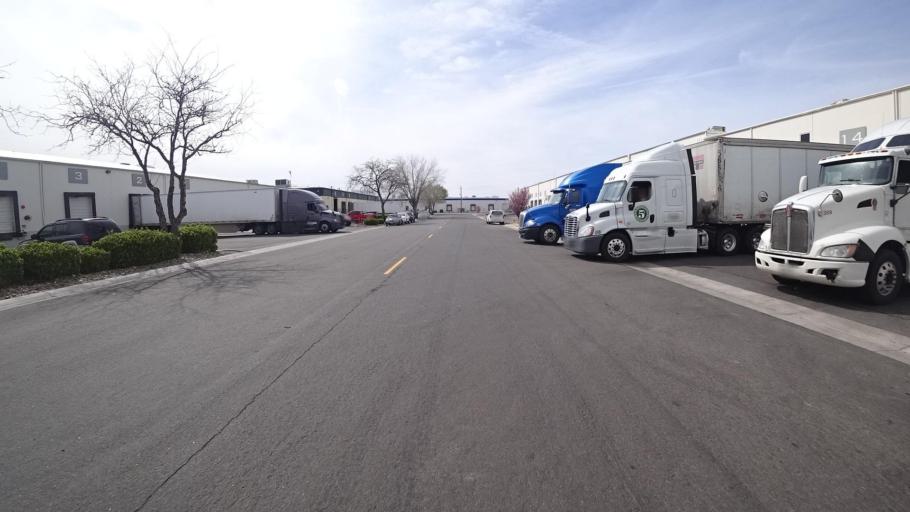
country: US
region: Nevada
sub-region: Washoe County
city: Sparks
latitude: 39.5230
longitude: -119.7511
